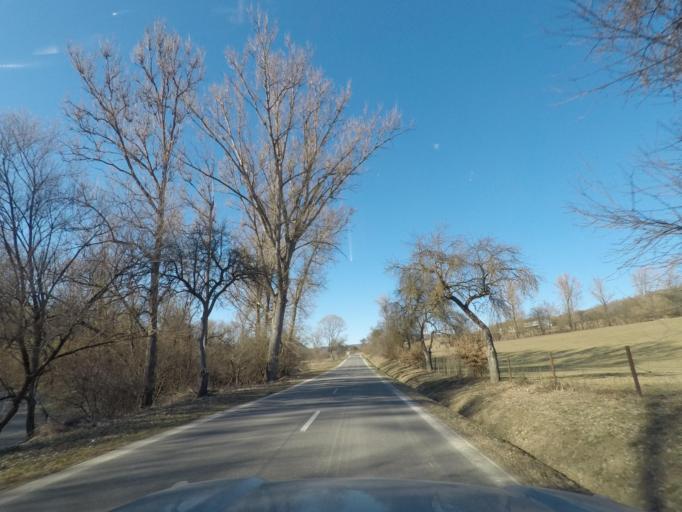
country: SK
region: Presovsky
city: Snina
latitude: 49.0552
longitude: 22.1719
